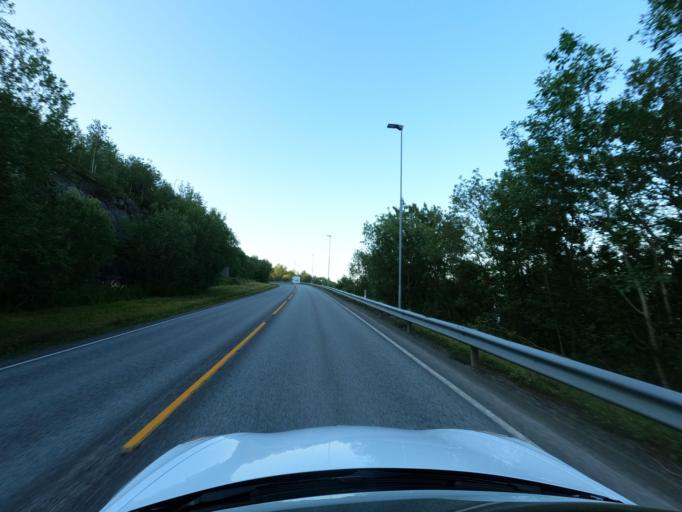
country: NO
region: Troms
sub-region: Harstad
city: Harstad
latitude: 68.7505
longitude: 16.5649
